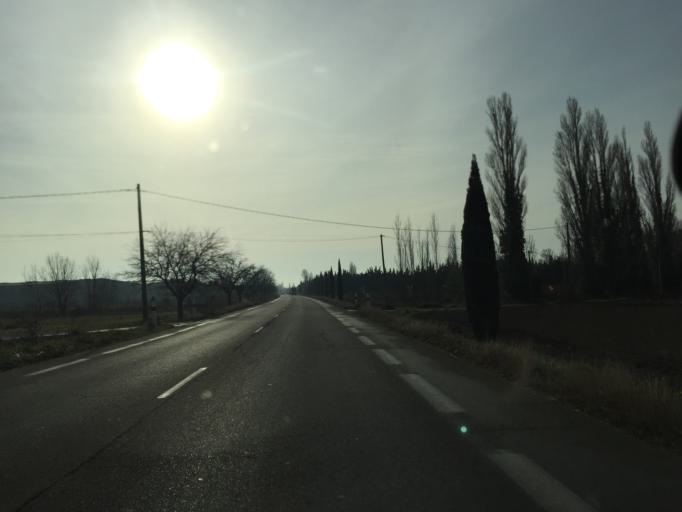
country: FR
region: Provence-Alpes-Cote d'Azur
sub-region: Departement du Vaucluse
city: Camaret-sur-Aigues
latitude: 44.1685
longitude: 4.8568
